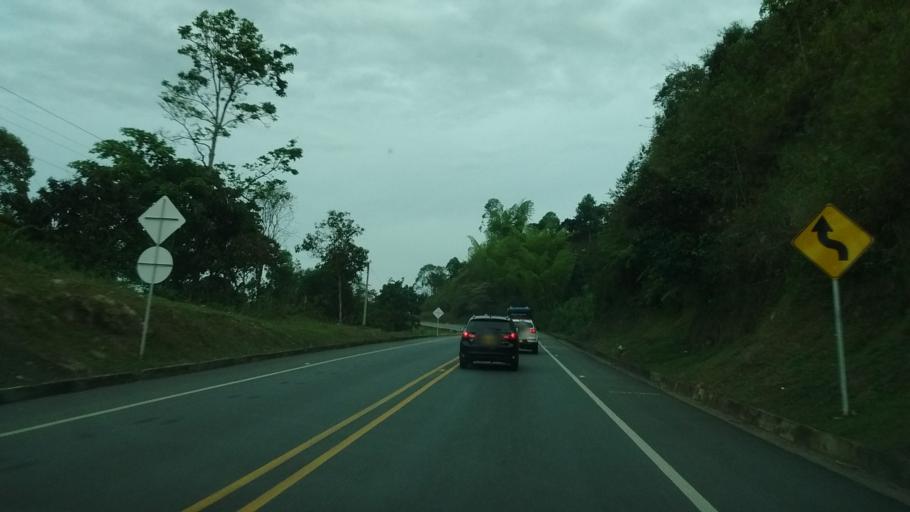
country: CO
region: Cauca
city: Morales
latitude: 2.7272
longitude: -76.5438
